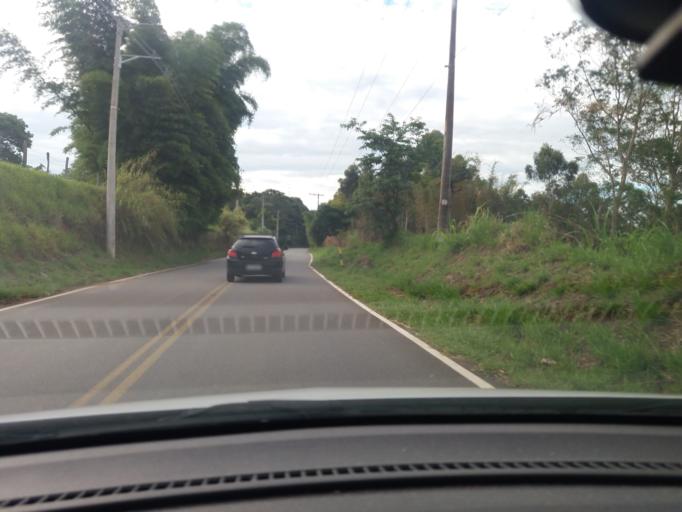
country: BR
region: Sao Paulo
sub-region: Bom Jesus Dos Perdoes
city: Bom Jesus dos Perdoes
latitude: -23.1550
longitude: -46.4530
